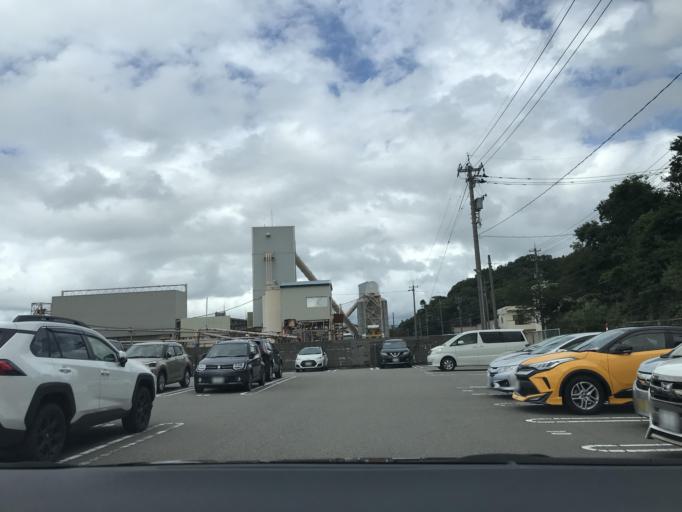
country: JP
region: Ishikawa
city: Tsubata
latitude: 36.6561
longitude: 136.7302
